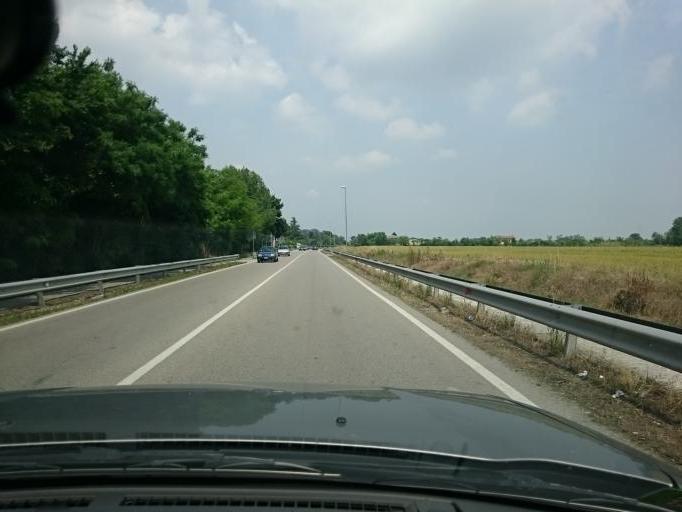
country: IT
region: Veneto
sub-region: Provincia di Padova
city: Campagnola
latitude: 45.2834
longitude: 11.9950
